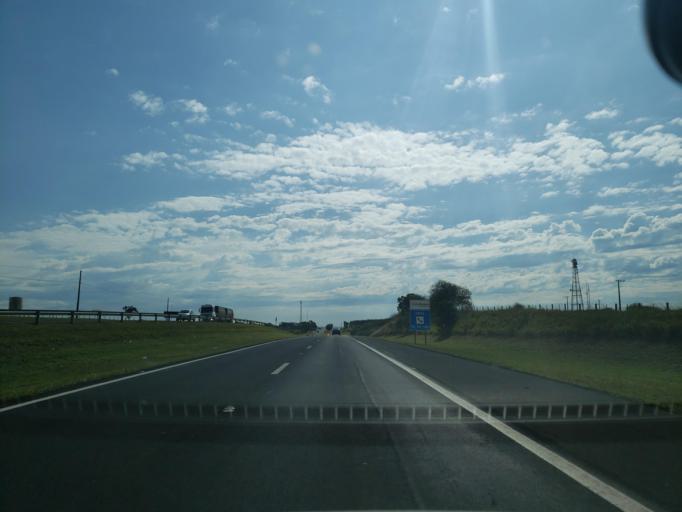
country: BR
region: Sao Paulo
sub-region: Pirajui
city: Pirajui
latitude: -22.0050
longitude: -49.4264
